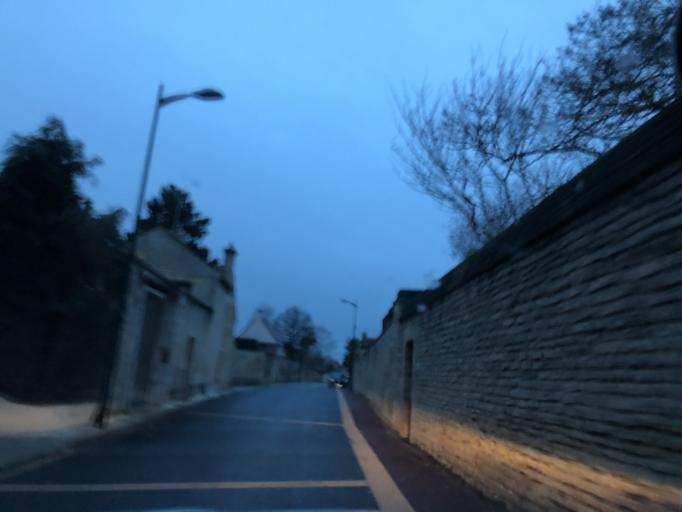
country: FR
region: Lower Normandy
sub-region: Departement du Calvados
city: Mathieu
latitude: 49.2518
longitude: -0.3666
